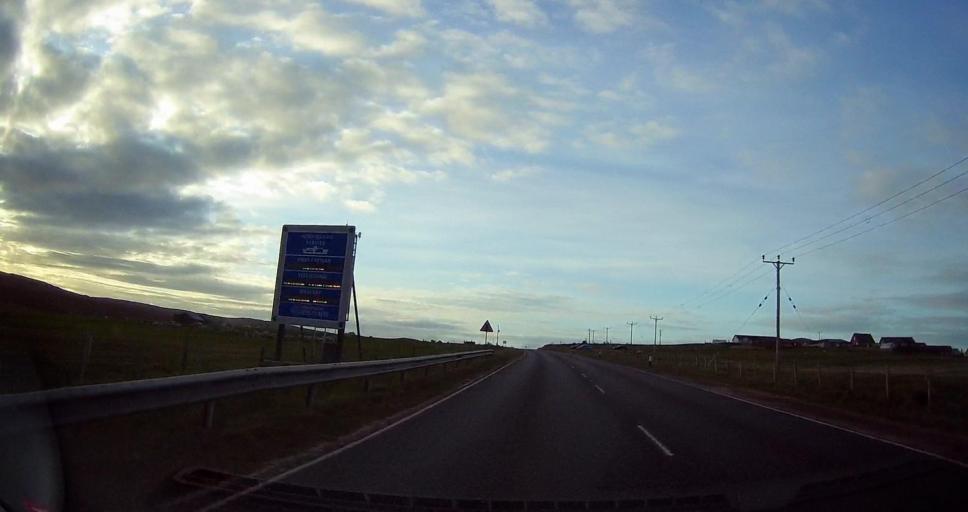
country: GB
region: Scotland
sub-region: Shetland Islands
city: Lerwick
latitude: 60.1969
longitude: -1.2320
